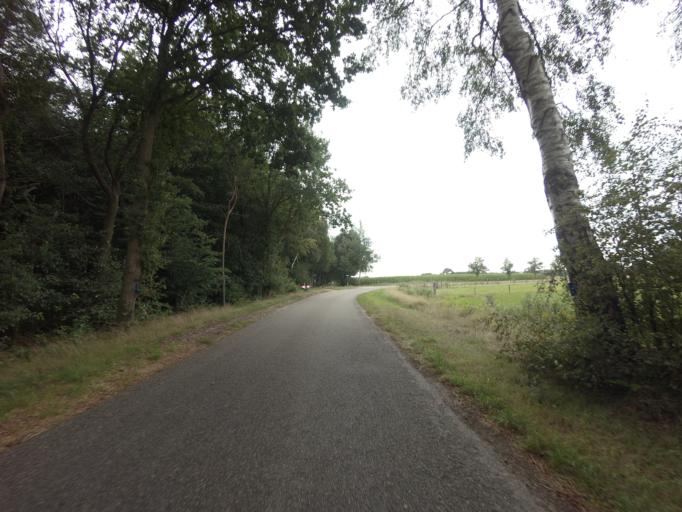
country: NL
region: Gelderland
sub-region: Gemeente Lochem
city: Laren
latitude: 52.2991
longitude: 6.3700
